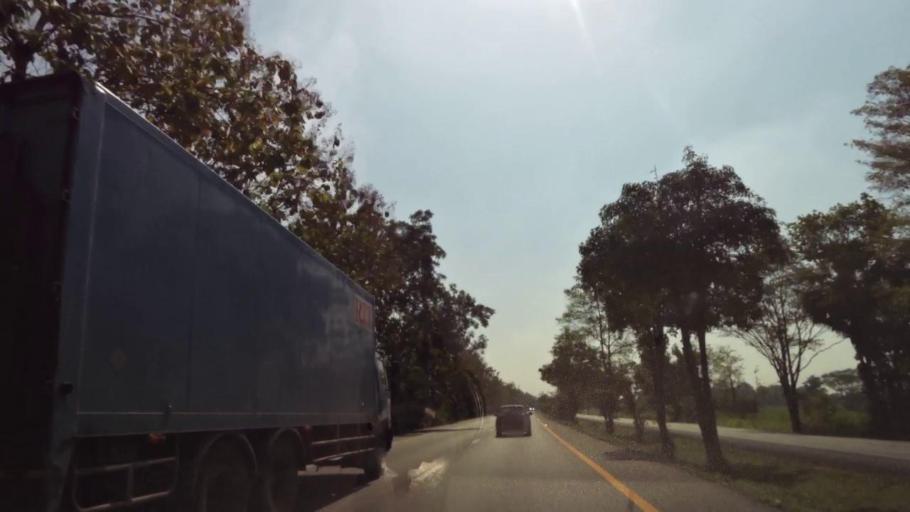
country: TH
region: Phichit
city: Bueng Na Rang
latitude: 16.0578
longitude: 100.1224
